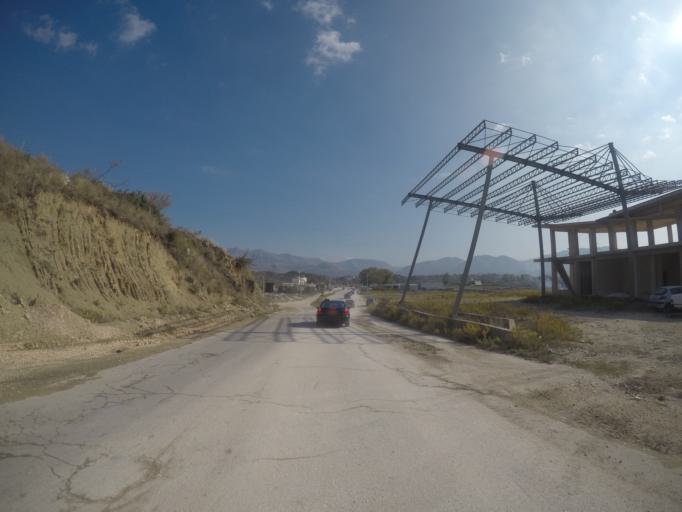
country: AL
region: Vlore
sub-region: Rrethi i Sarandes
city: Sarande
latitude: 39.8792
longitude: 20.0322
